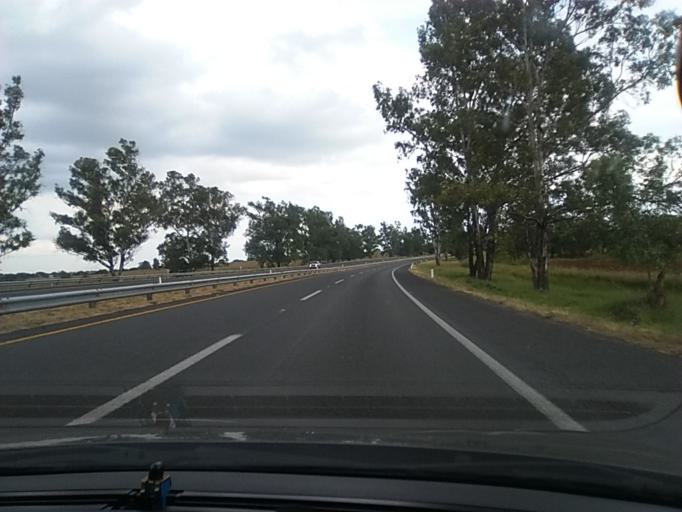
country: MX
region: Jalisco
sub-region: Ocotlan
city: Joconoxtle (La Tuna)
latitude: 20.3732
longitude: -102.6604
